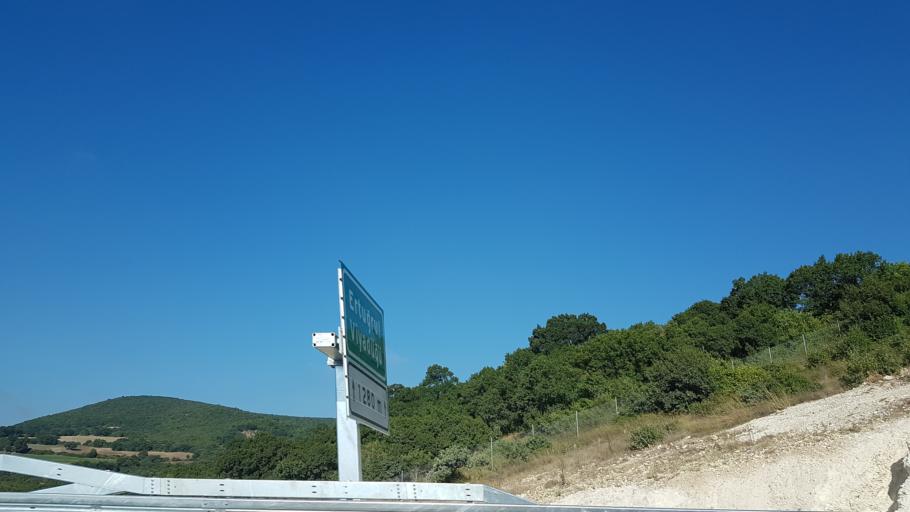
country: TR
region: Balikesir
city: Ertugrul
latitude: 39.5814
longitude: 27.6970
